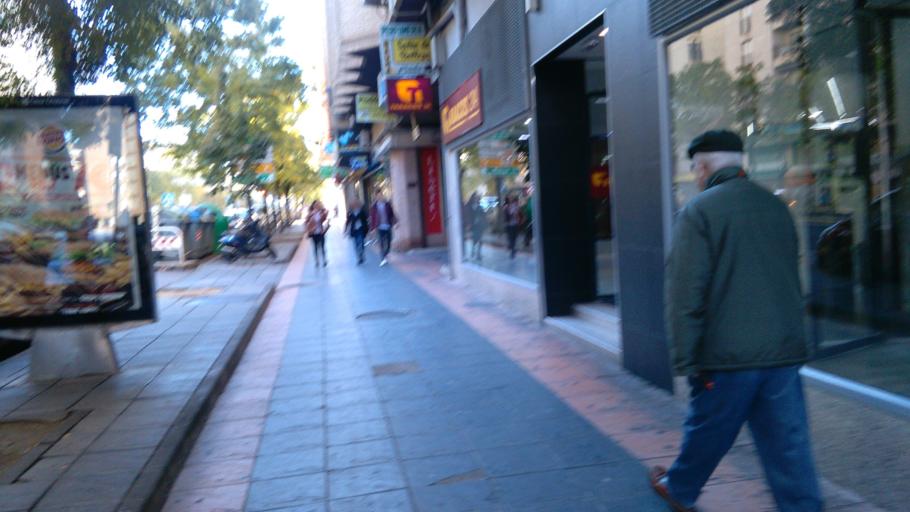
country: ES
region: Extremadura
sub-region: Provincia de Caceres
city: Caceres
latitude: 39.4678
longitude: -6.3798
